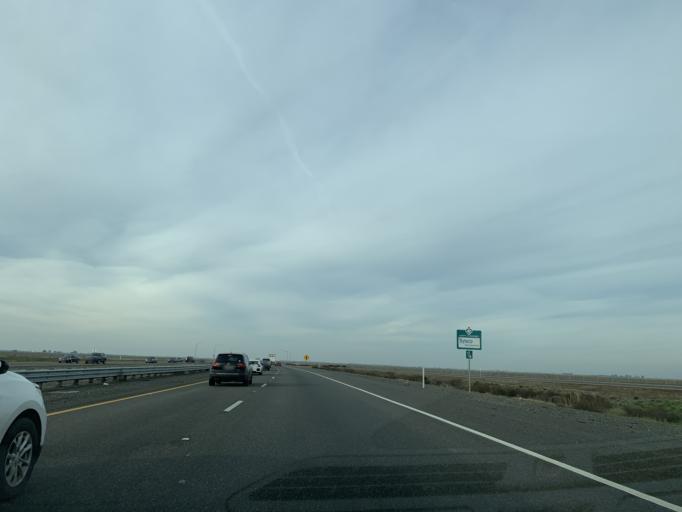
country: US
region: California
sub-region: Sacramento County
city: Elverta
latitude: 38.7523
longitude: -121.5410
